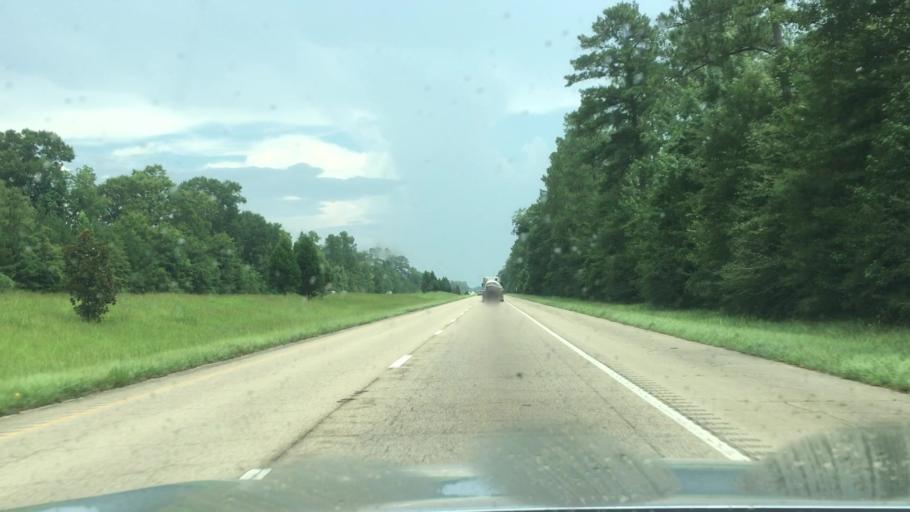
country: US
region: Mississippi
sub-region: Lamar County
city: Lumberton
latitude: 31.0191
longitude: -89.4093
